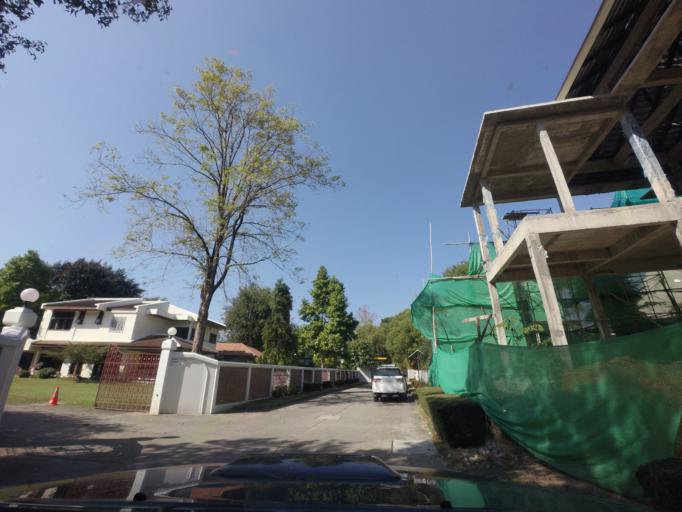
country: TH
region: Chiang Mai
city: Chiang Mai
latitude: 18.7694
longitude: 99.0034
